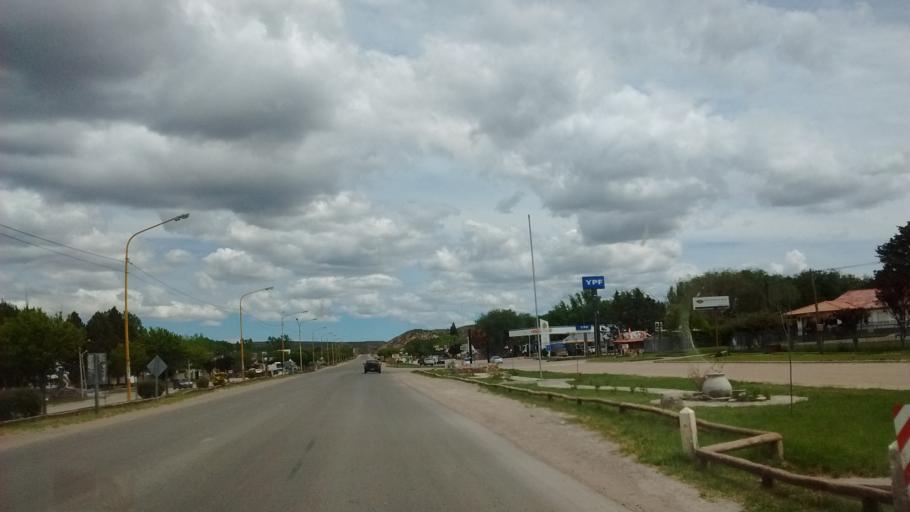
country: AR
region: Neuquen
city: Piedra del Aguila
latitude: -40.0477
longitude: -70.0755
